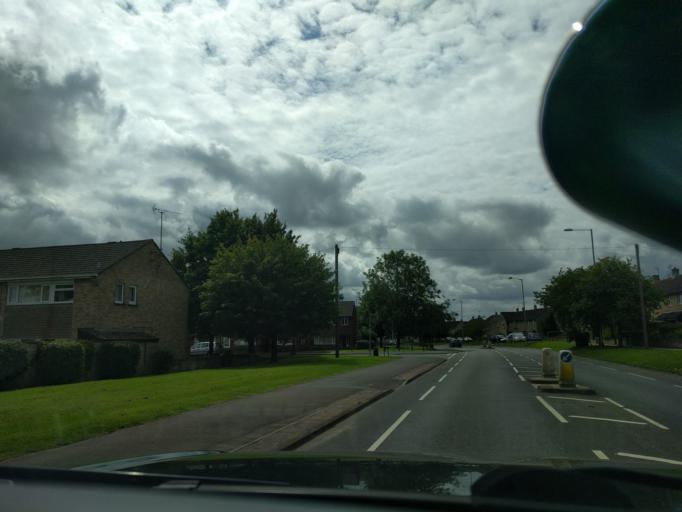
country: GB
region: England
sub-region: Wiltshire
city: Chippenham
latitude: 51.4647
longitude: -2.1374
